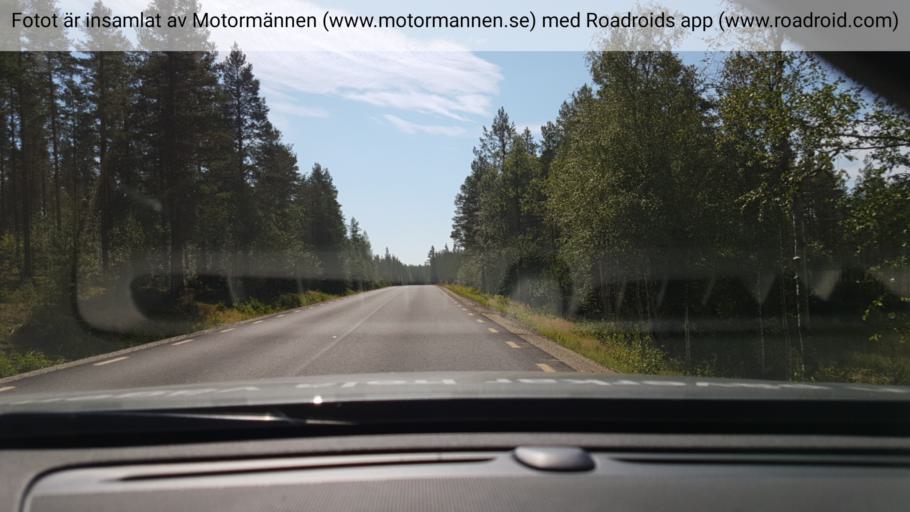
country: SE
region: Vaesterbotten
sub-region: Vindelns Kommun
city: Vindeln
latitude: 64.4370
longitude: 19.3475
